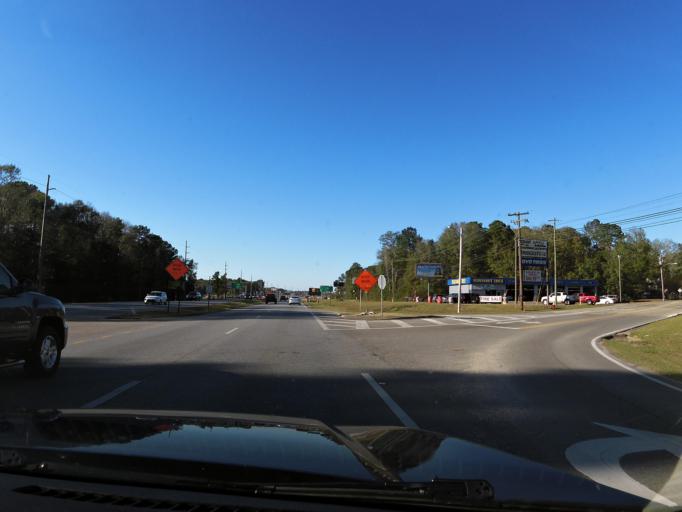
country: US
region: Alabama
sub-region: Houston County
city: Dothan
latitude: 31.2043
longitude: -85.4201
